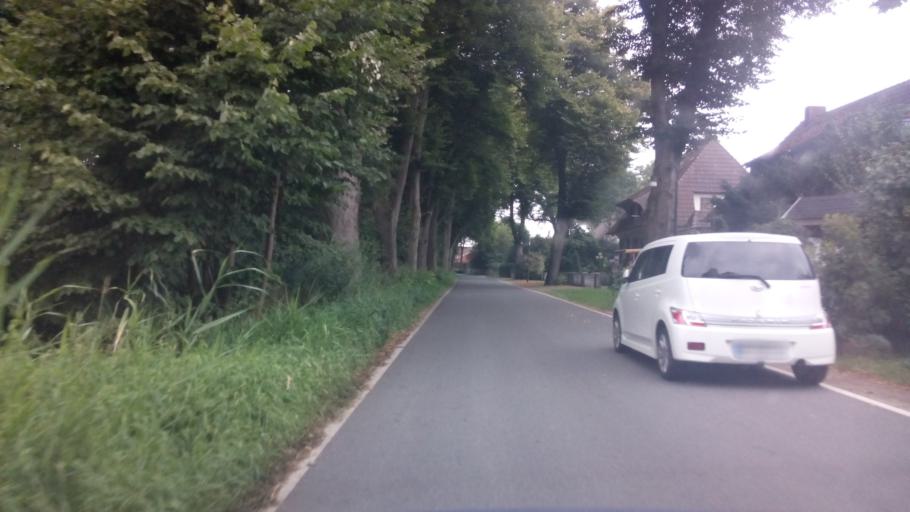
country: DE
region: Lower Saxony
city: Lilienthal
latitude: 53.1247
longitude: 8.8757
